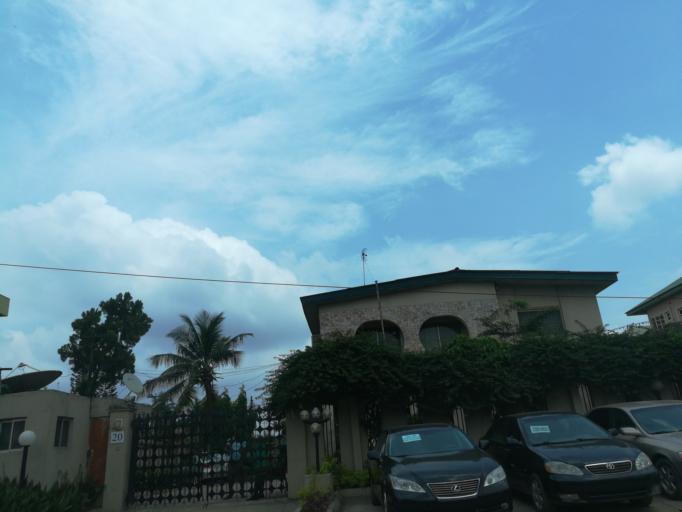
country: NG
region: Lagos
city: Oshodi
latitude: 6.5467
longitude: 3.3299
